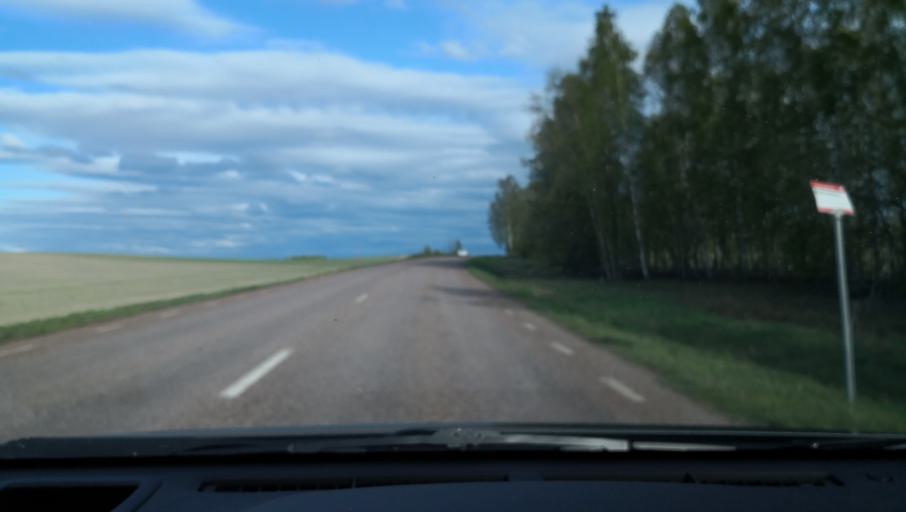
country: SE
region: Dalarna
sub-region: Hedemora Kommun
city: Hedemora
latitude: 60.2888
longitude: 15.9065
